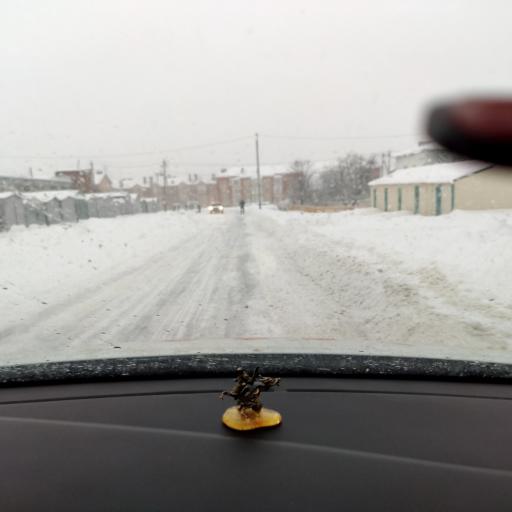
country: RU
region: Tatarstan
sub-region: Arskiy Rayon
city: Arsk
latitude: 56.0991
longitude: 49.8759
